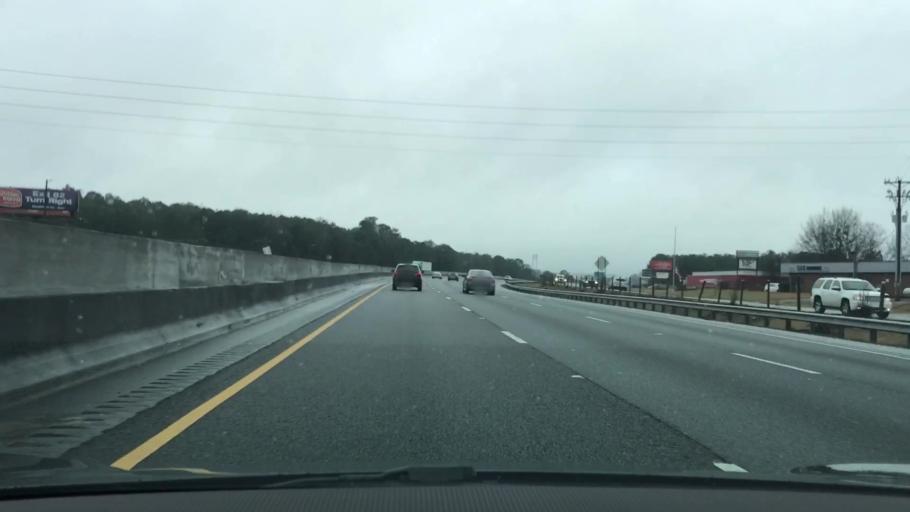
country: US
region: Georgia
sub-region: Rockdale County
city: Conyers
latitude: 33.6319
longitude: -83.9702
